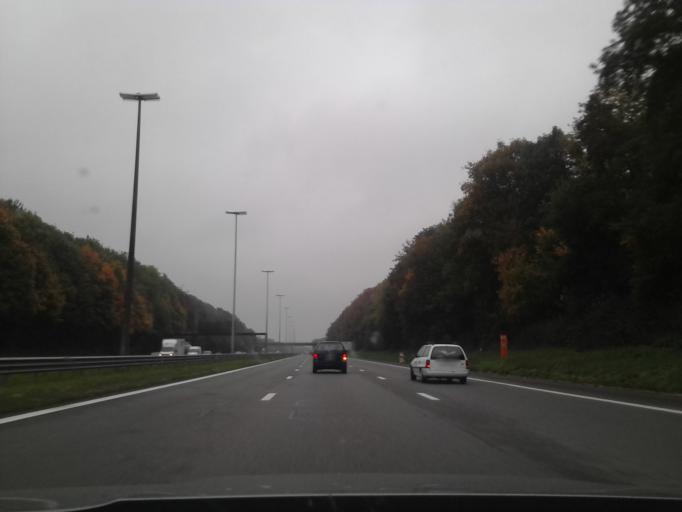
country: BE
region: Wallonia
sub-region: Province du Brabant Wallon
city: Ittre
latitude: 50.6374
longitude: 4.3073
